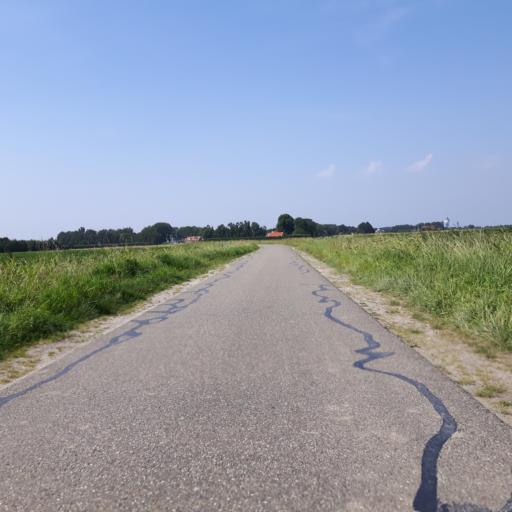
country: NL
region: Zeeland
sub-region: Gemeente Goes
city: Goes
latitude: 51.4800
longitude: 3.9245
